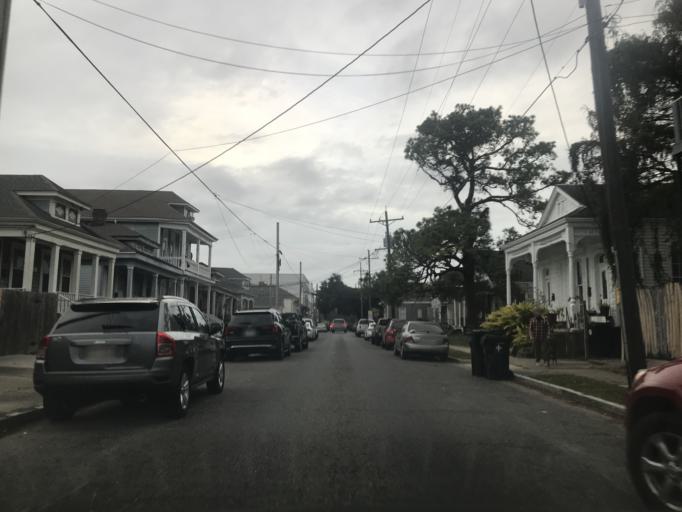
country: US
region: Louisiana
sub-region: Orleans Parish
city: New Orleans
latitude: 29.9669
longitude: -90.0915
